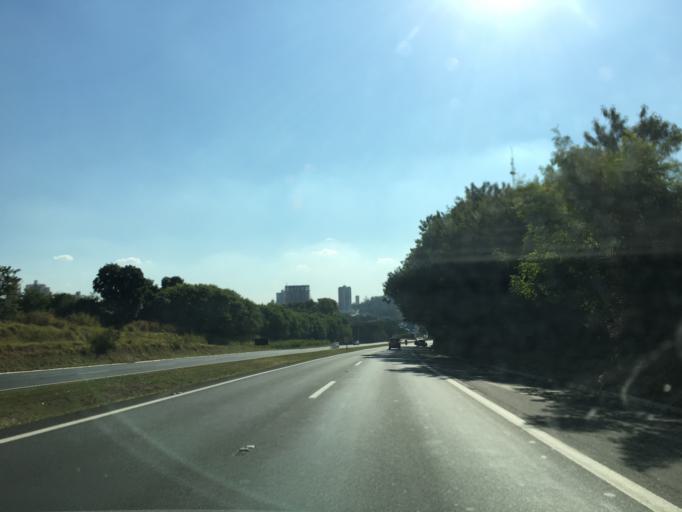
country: BR
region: Sao Paulo
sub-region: Piracicaba
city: Piracicaba
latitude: -22.7196
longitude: -47.6200
